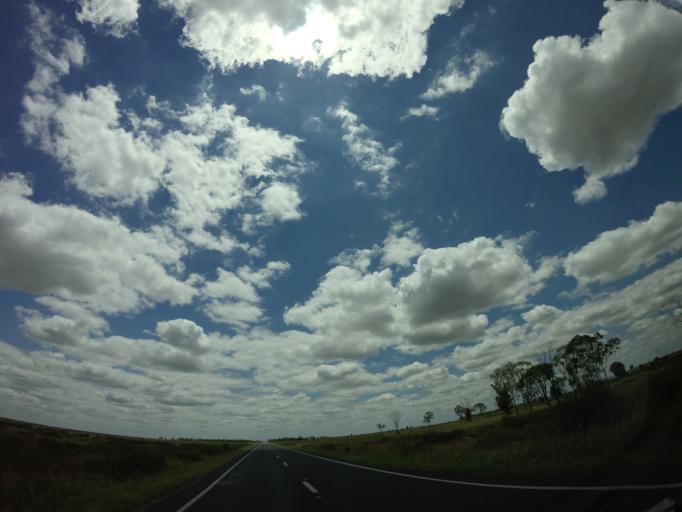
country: AU
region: New South Wales
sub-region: Moree Plains
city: Boggabilla
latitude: -28.6936
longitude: 150.2907
